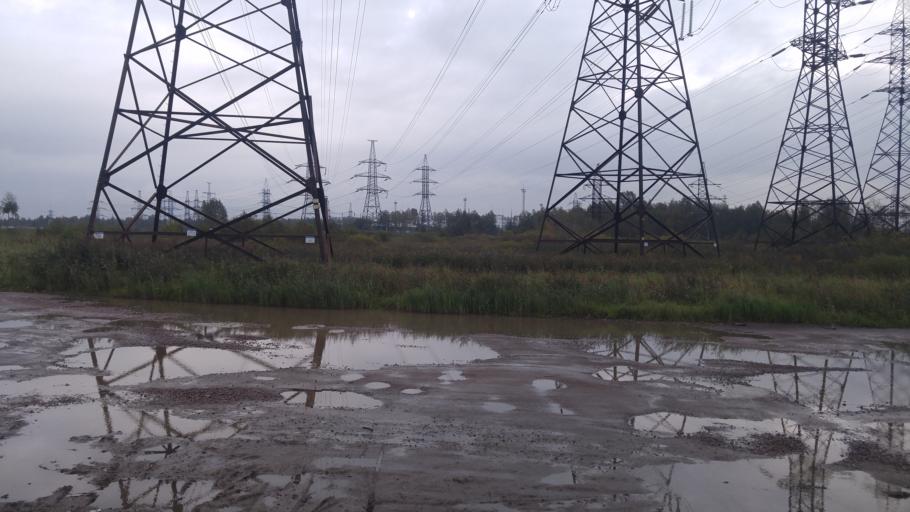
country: RU
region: St.-Petersburg
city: Metallostroy
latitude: 59.7770
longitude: 30.5563
